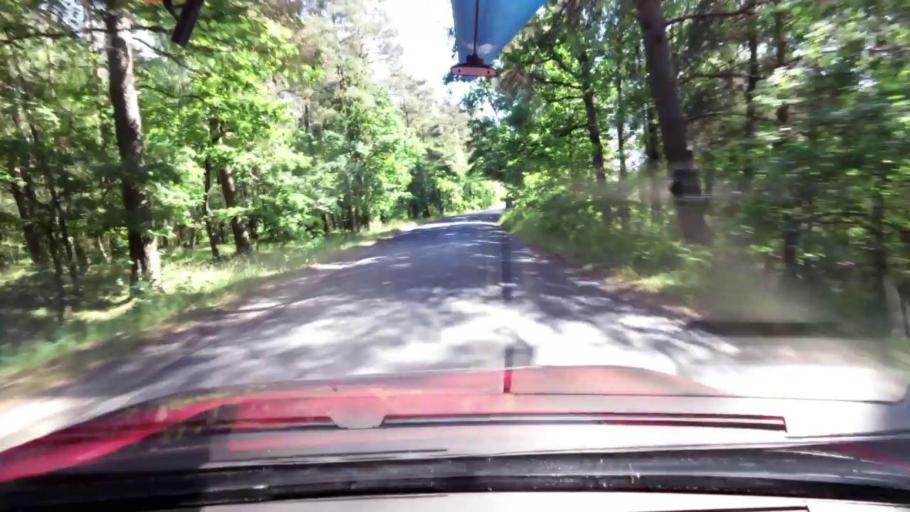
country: PL
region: Pomeranian Voivodeship
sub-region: Powiat slupski
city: Kepice
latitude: 54.3097
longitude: 16.9624
